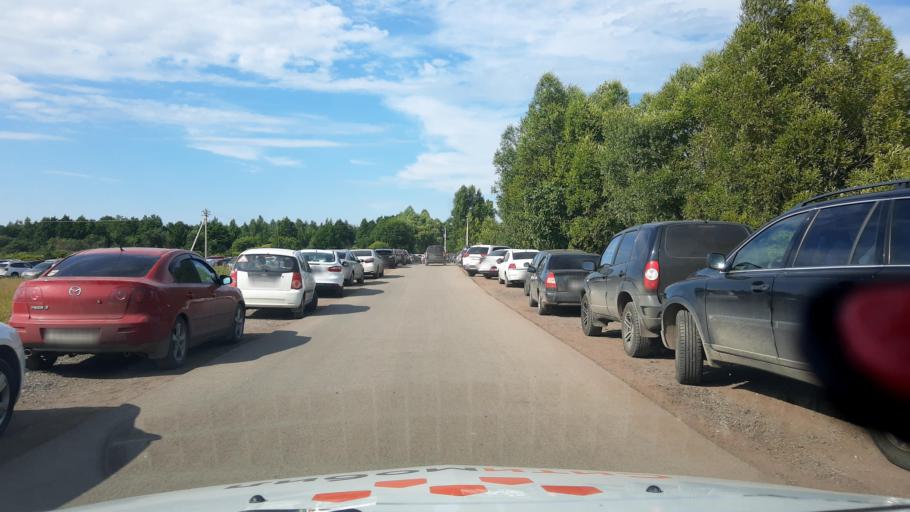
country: RU
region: Bashkortostan
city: Blagoveshchensk
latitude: 54.9666
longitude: 55.8133
